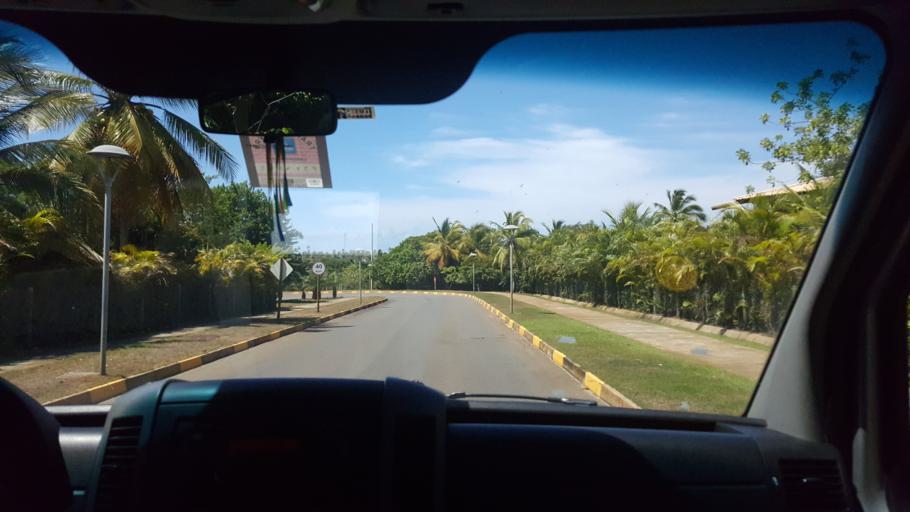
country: BR
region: Bahia
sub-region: Mata De Sao Joao
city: Mata de Sao Joao
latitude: -12.4820
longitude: -37.9575
